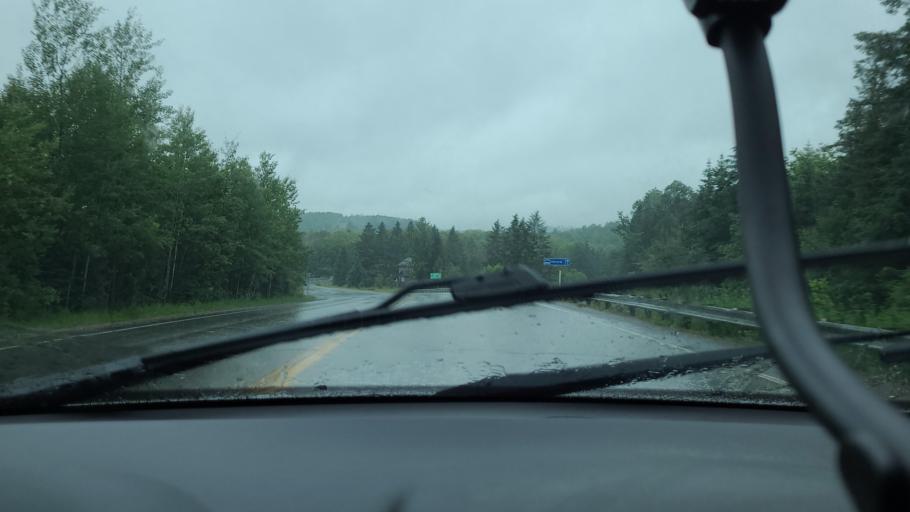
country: CA
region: Quebec
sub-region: Outaouais
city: Saint-Andre-Avellin
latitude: 45.8297
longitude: -75.0672
